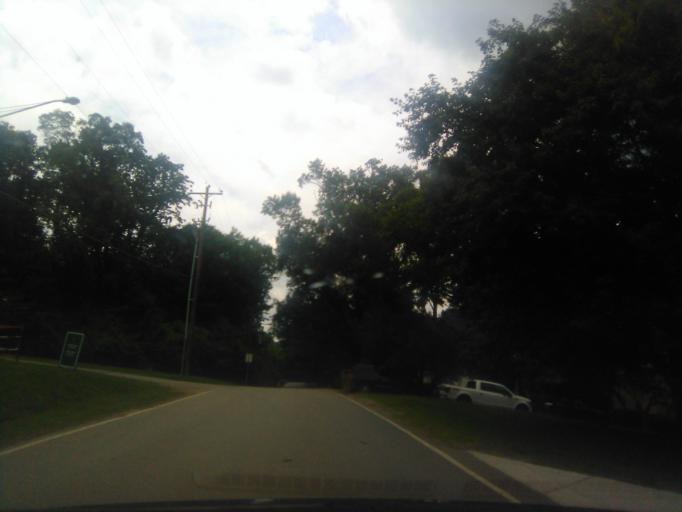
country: US
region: Tennessee
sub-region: Davidson County
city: Belle Meade
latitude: 36.0910
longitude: -86.8751
